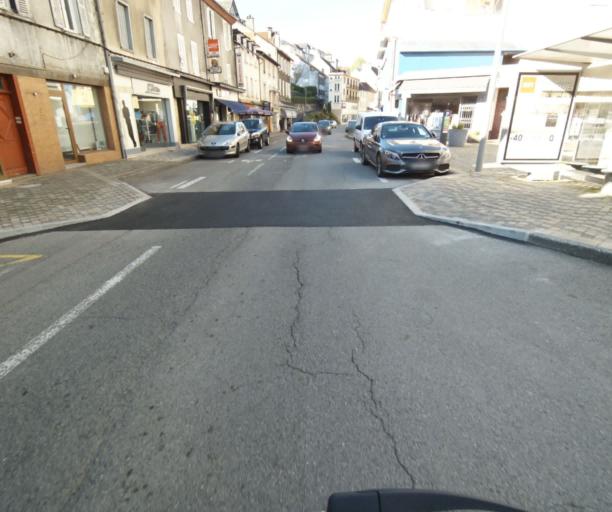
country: FR
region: Limousin
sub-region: Departement de la Correze
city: Tulle
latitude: 45.2618
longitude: 1.7603
